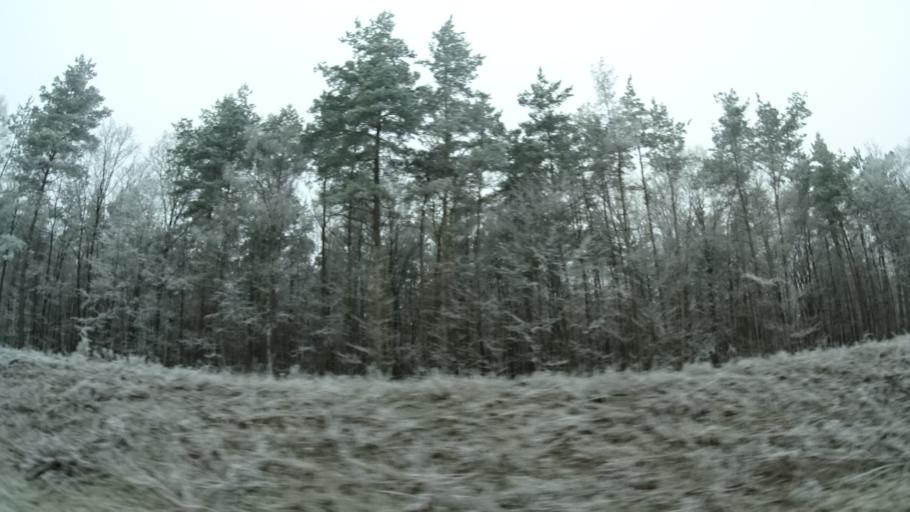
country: DE
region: Bavaria
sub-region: Regierungsbezirk Unterfranken
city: Grosslangheim
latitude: 49.7805
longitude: 10.2075
